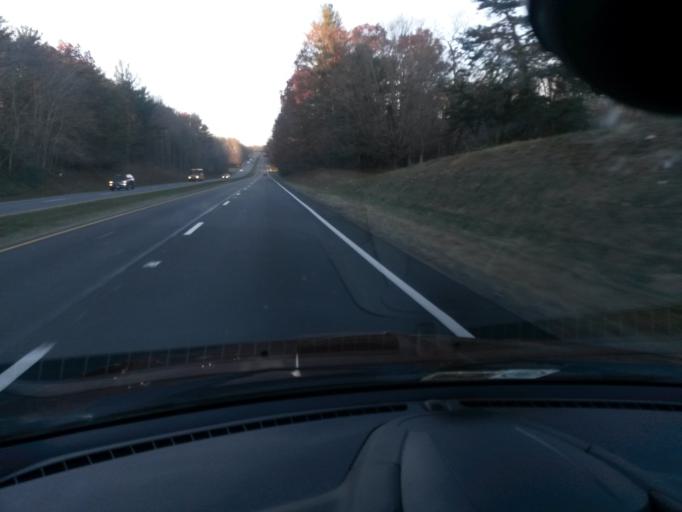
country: US
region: Virginia
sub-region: Franklin County
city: Henry Fork
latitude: 36.9763
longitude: -79.8725
